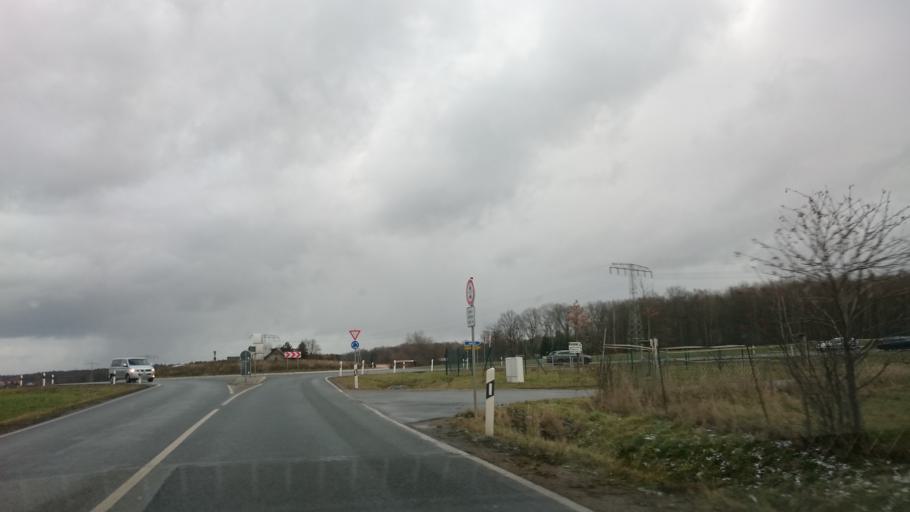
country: DE
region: Saxony
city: Hartmannsdorf
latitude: 50.7312
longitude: 12.4101
